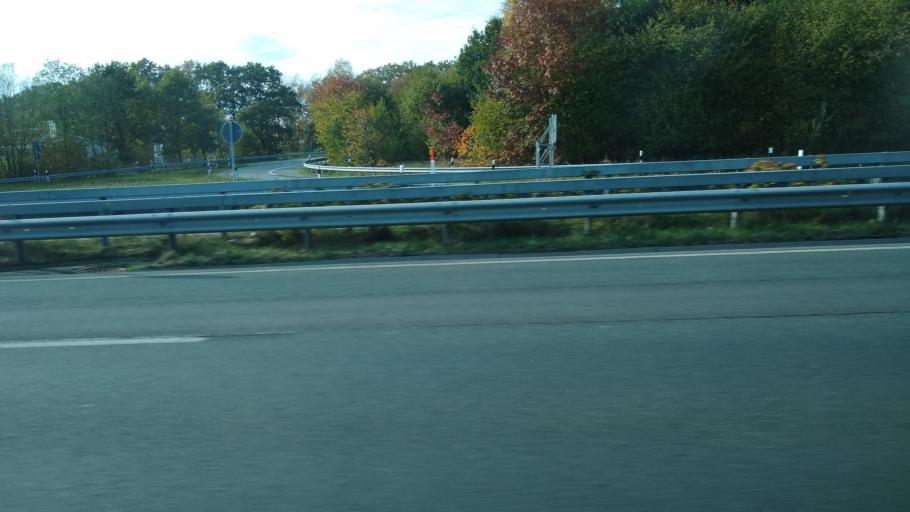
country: DE
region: Lower Saxony
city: Oldenburg
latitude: 53.1842
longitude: 8.2267
